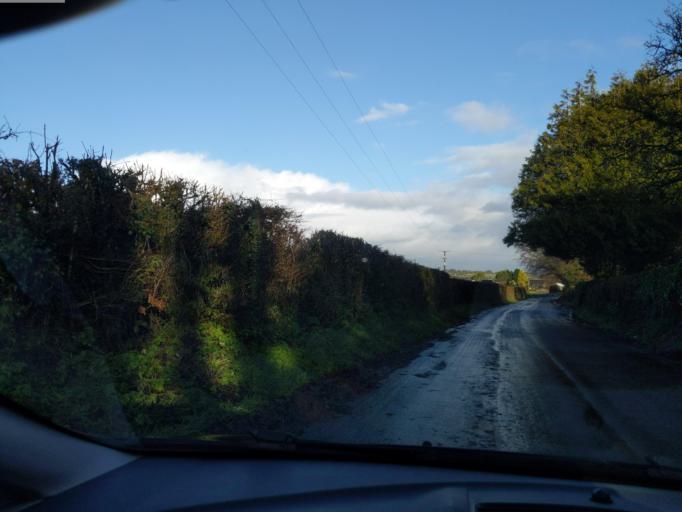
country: GB
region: England
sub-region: Devon
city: Okehampton
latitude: 50.7176
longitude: -4.0446
